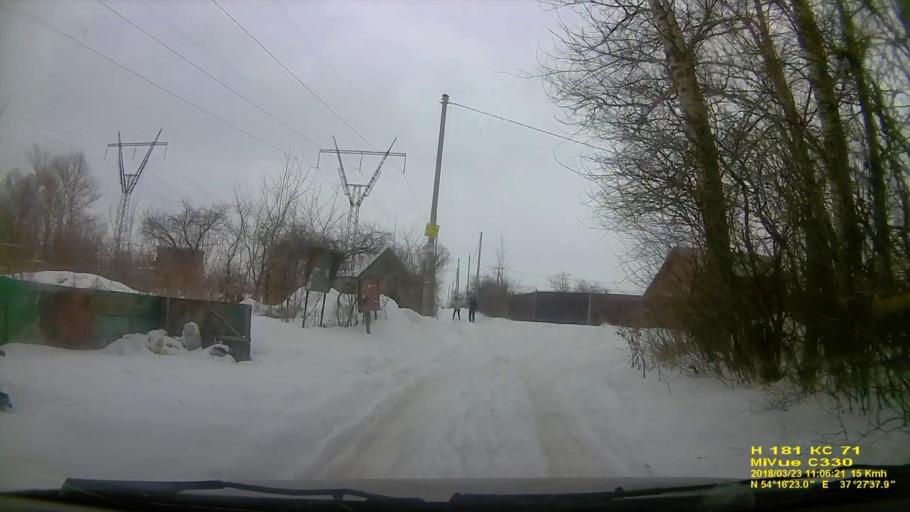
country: RU
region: Tula
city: Leninskiy
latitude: 54.2726
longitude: 37.4603
